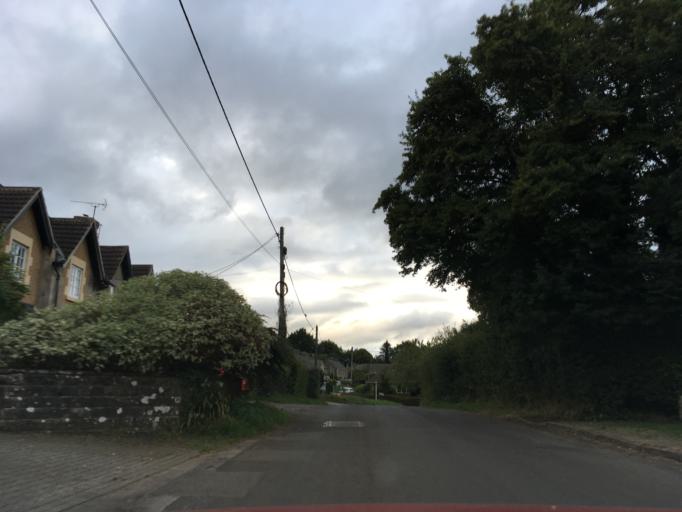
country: GB
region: England
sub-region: Wiltshire
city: Biddestone
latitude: 51.4583
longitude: -2.2031
